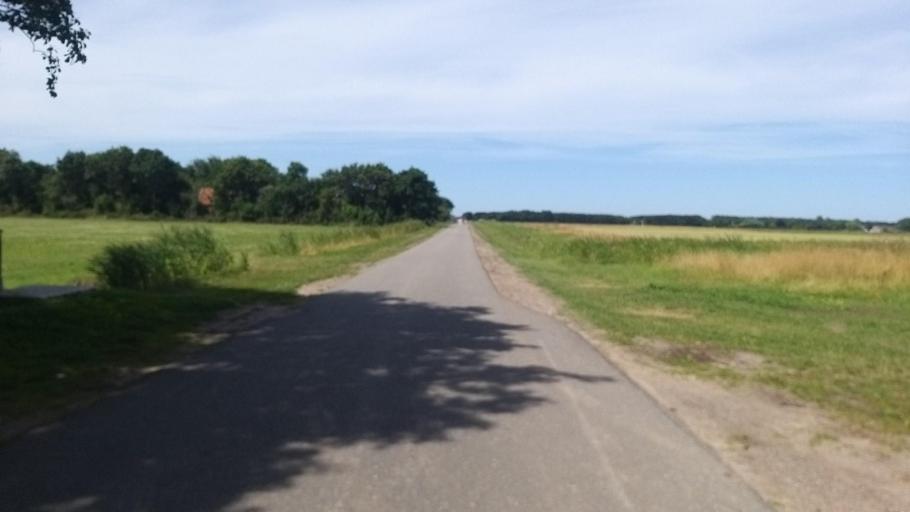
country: NL
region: North Holland
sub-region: Gemeente Texel
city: Den Burg
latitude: 53.1422
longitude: 4.8725
